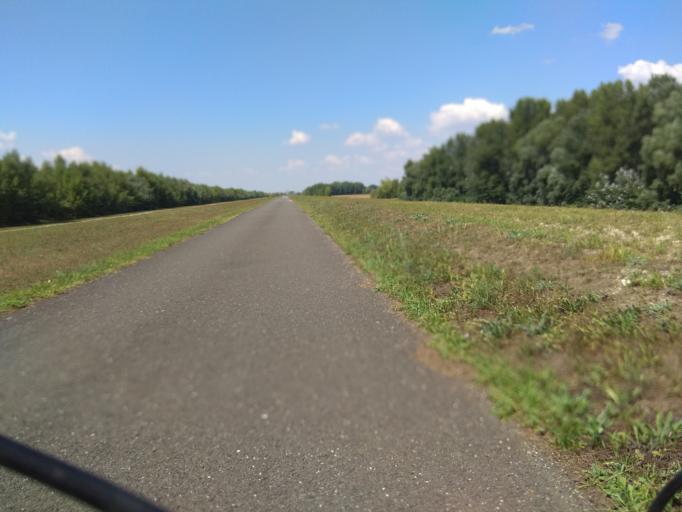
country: SK
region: Trnavsky
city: Gabcikovo
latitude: 47.8539
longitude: 17.5730
